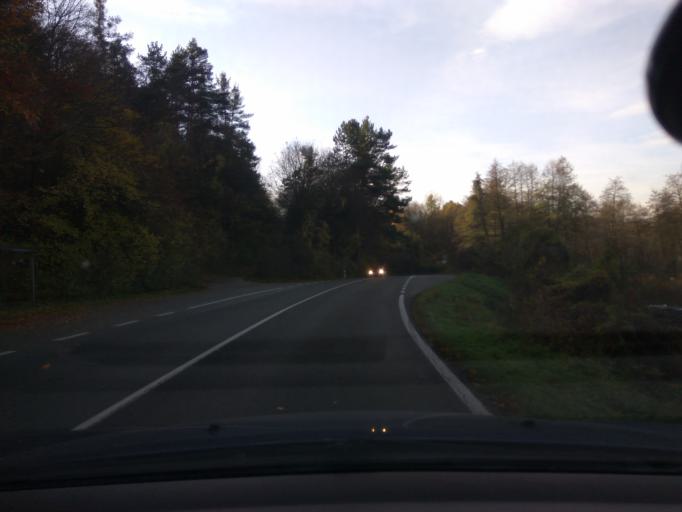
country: SK
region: Nitriansky
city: Brezova pod Bradlom
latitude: 48.6345
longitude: 17.5005
